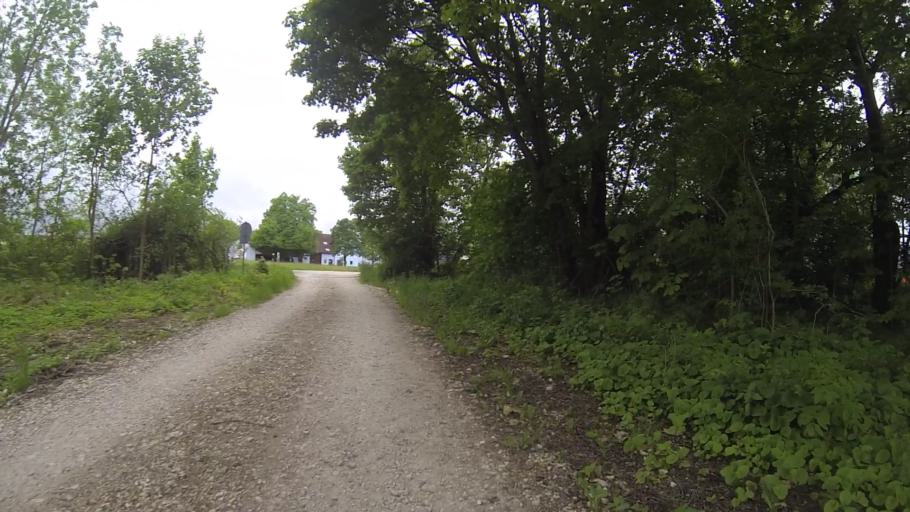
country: DE
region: Baden-Wuerttemberg
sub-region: Regierungsbezirk Stuttgart
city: Bartholoma
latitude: 48.7801
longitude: 9.9838
